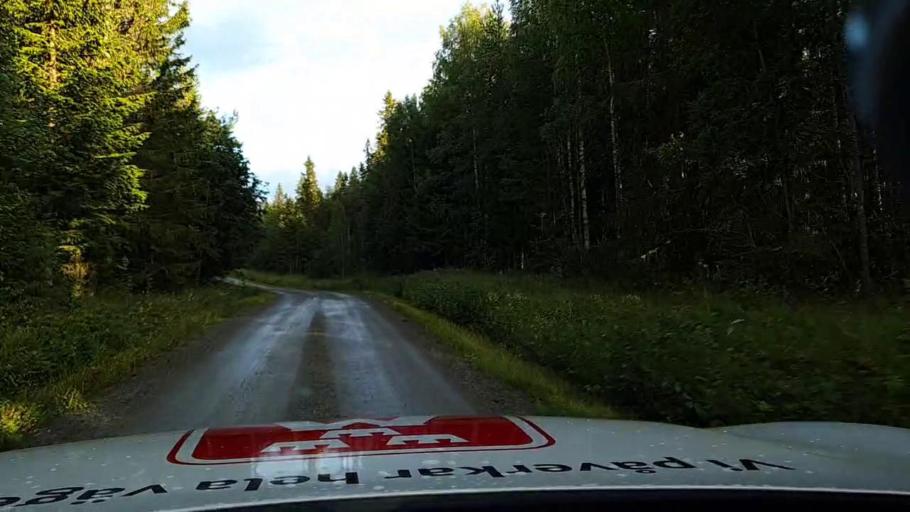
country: SE
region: Jaemtland
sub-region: Bergs Kommun
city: Hoverberg
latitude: 62.8522
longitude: 14.5387
